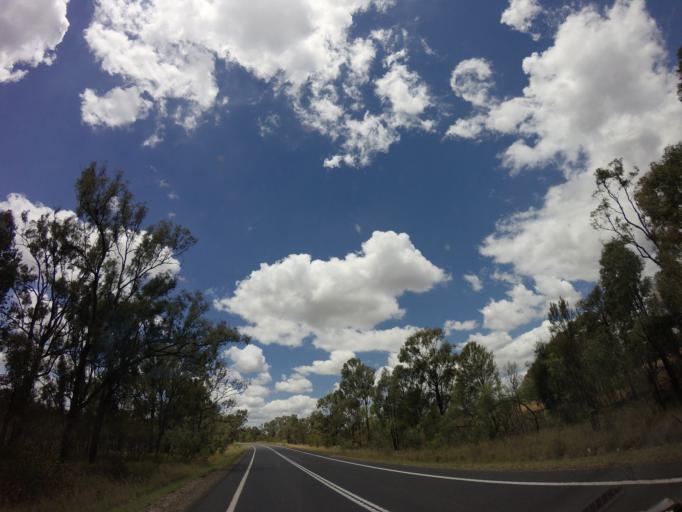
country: AU
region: Queensland
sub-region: Toowoomba
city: Oakey
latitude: -27.9176
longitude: 151.1767
